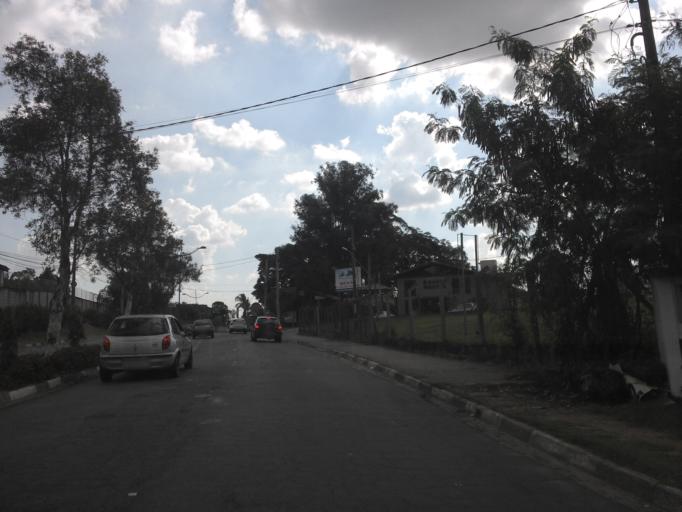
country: BR
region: Sao Paulo
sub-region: Vinhedo
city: Vinhedo
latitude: -23.0272
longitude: -46.9903
